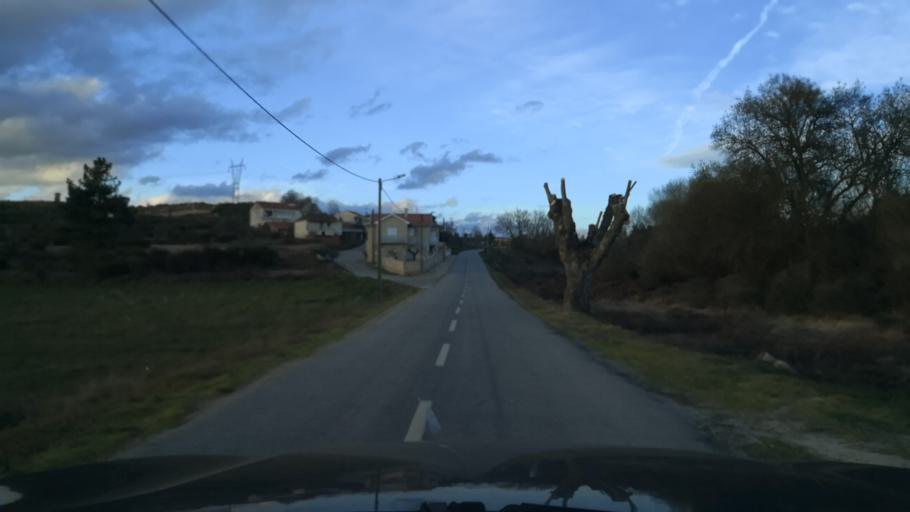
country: PT
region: Braganca
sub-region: Carrazeda de Ansiaes
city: Carrazeda de Anciaes
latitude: 41.2135
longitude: -7.3191
